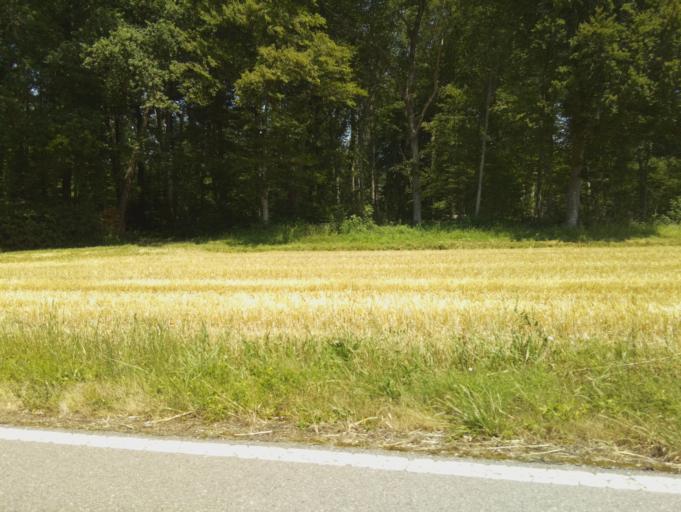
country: CH
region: Zurich
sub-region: Bezirk Andelfingen
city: Marthalen
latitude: 47.6280
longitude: 8.6696
